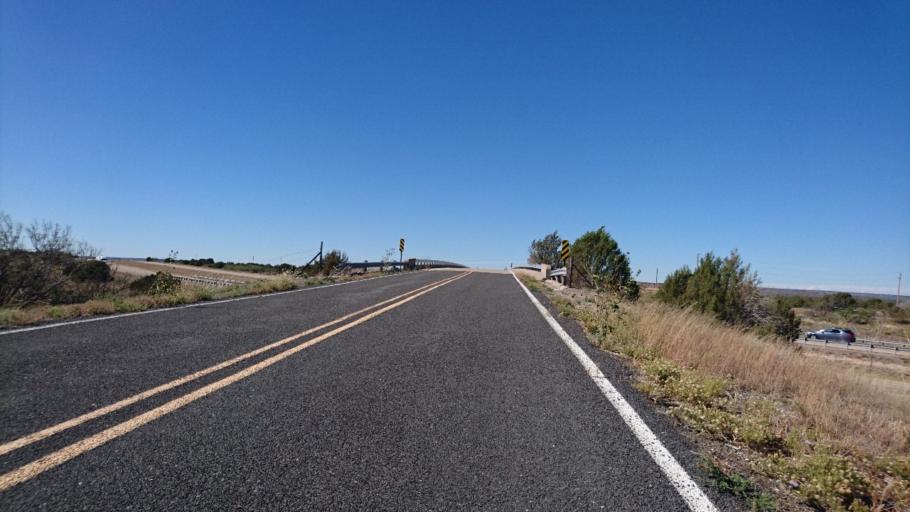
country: US
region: New Mexico
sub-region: Quay County
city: Tucumcari
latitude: 35.0663
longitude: -104.1785
